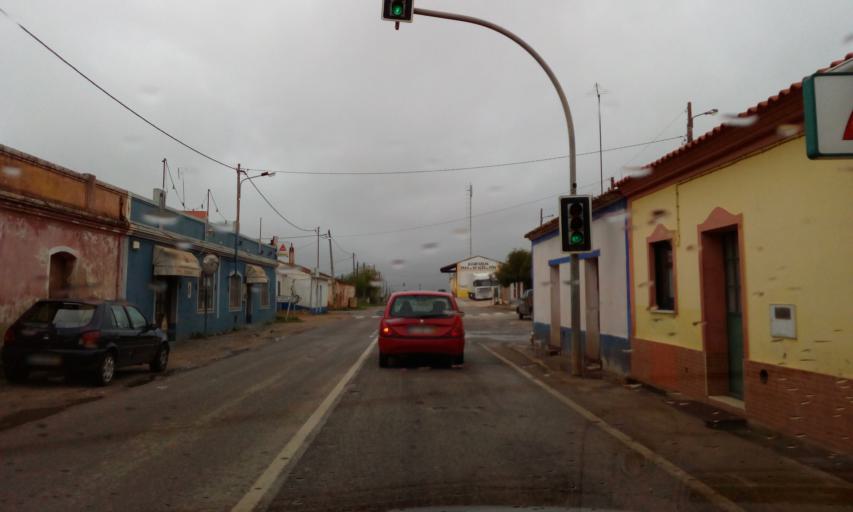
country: PT
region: Faro
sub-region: Albufeira
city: Guia
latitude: 37.1701
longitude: -8.3468
